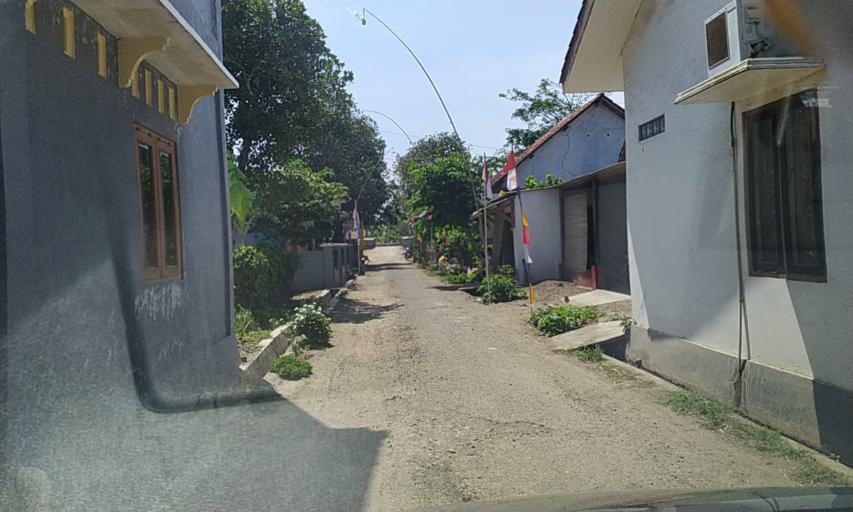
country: ID
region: Central Java
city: Rejanegara
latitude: -7.6659
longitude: 109.0569
